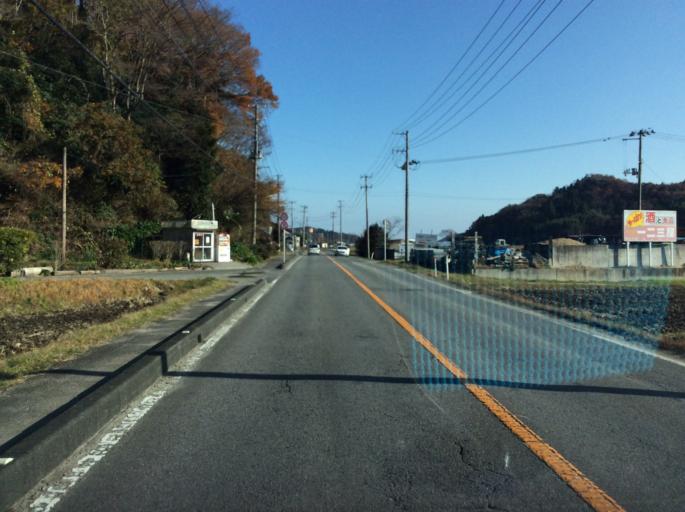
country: JP
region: Fukushima
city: Iwaki
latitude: 37.0341
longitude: 140.9222
